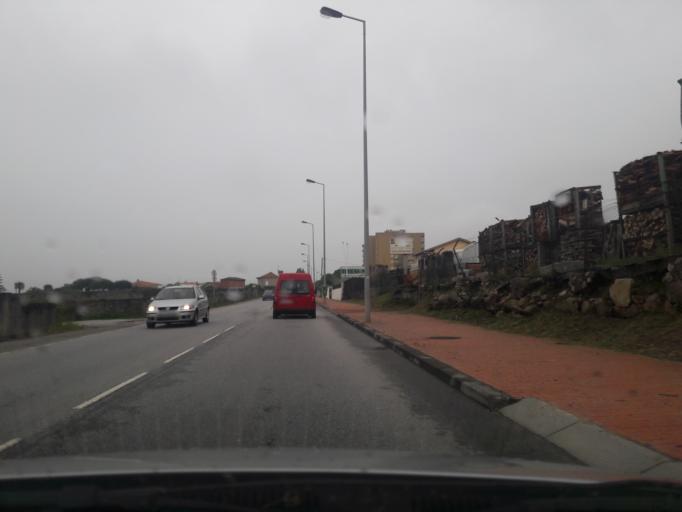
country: PT
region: Porto
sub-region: Vila do Conde
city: Arvore
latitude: 41.3397
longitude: -8.7306
